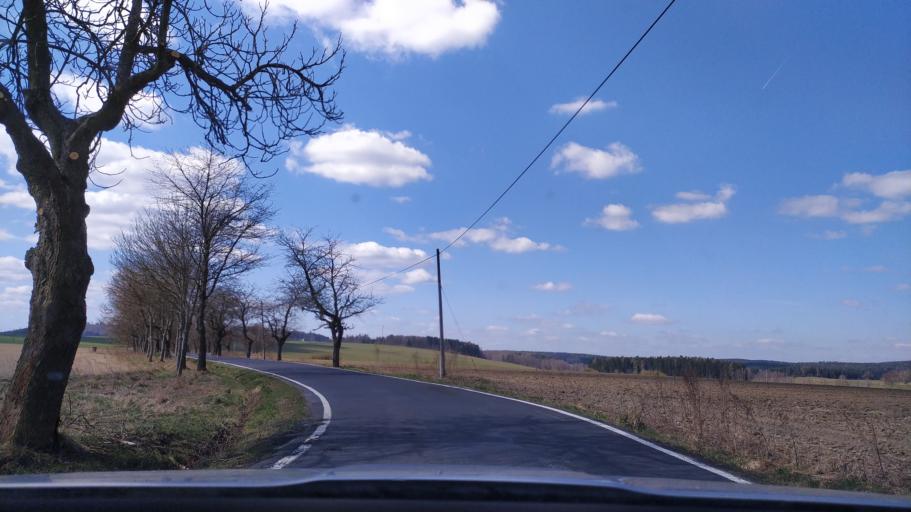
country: CZ
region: Karlovarsky
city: Hazlov
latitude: 50.1249
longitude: 12.2654
